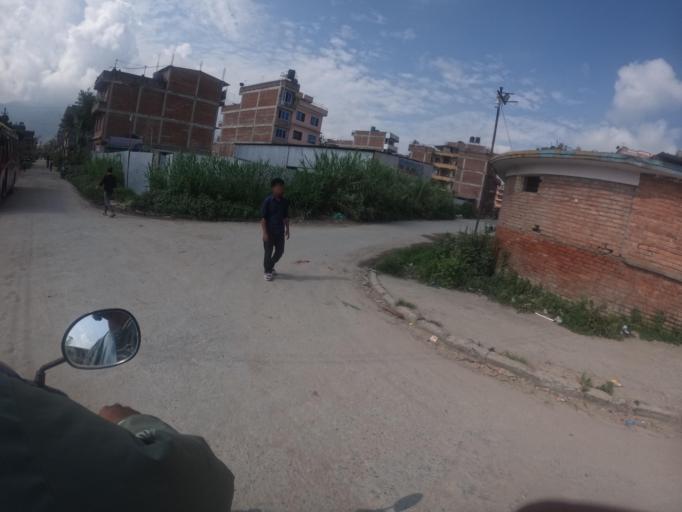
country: NP
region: Central Region
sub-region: Bagmati Zone
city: Bhaktapur
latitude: 27.6735
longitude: 85.4434
